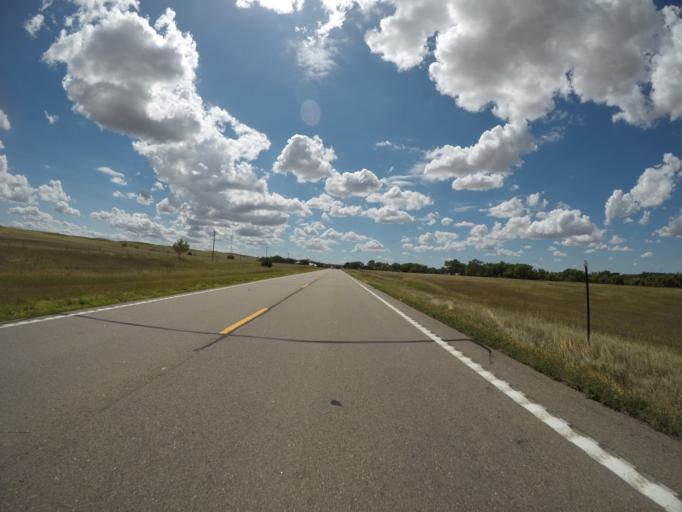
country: US
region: Nebraska
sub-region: Chase County
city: Imperial
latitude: 40.4118
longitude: -101.3550
